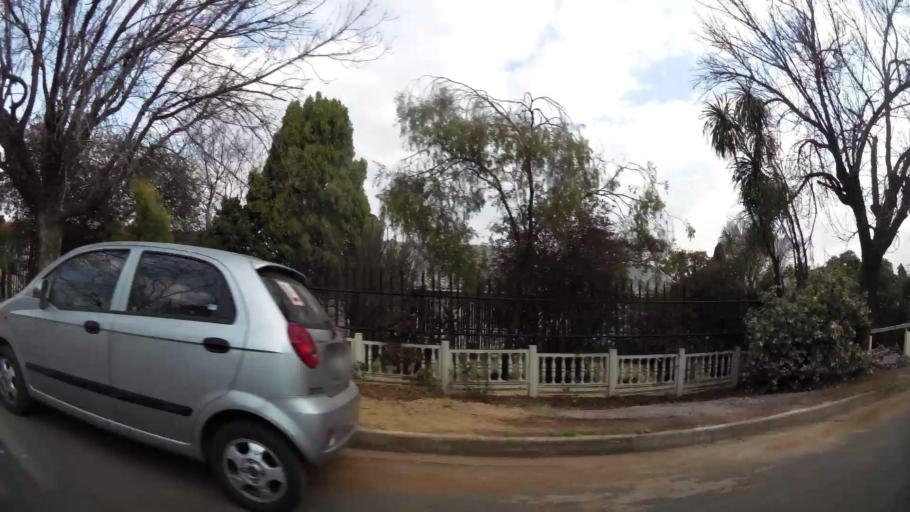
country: ZA
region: Gauteng
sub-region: City of Johannesburg Metropolitan Municipality
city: Modderfontein
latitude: -26.1391
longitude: 28.1865
